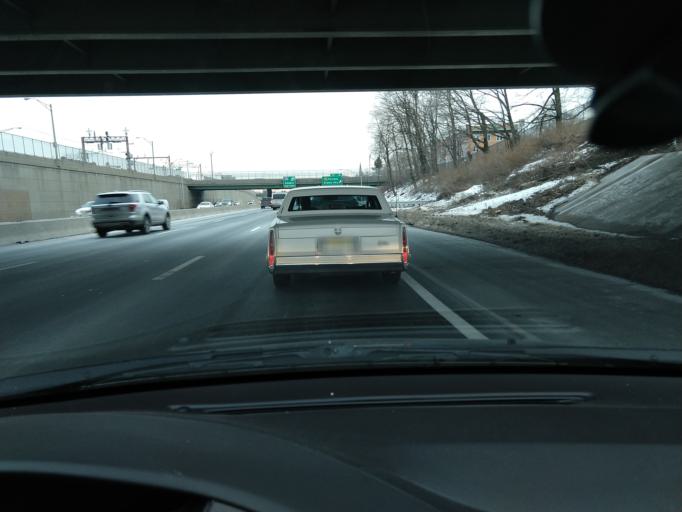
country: US
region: New Jersey
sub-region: Essex County
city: East Orange
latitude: 40.7626
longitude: -74.2151
